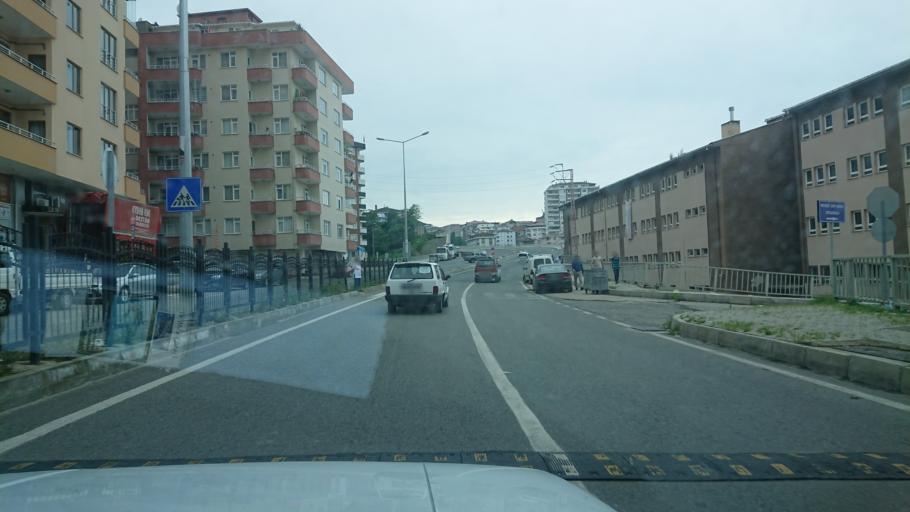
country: TR
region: Rize
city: Rize
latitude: 41.0210
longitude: 40.5294
